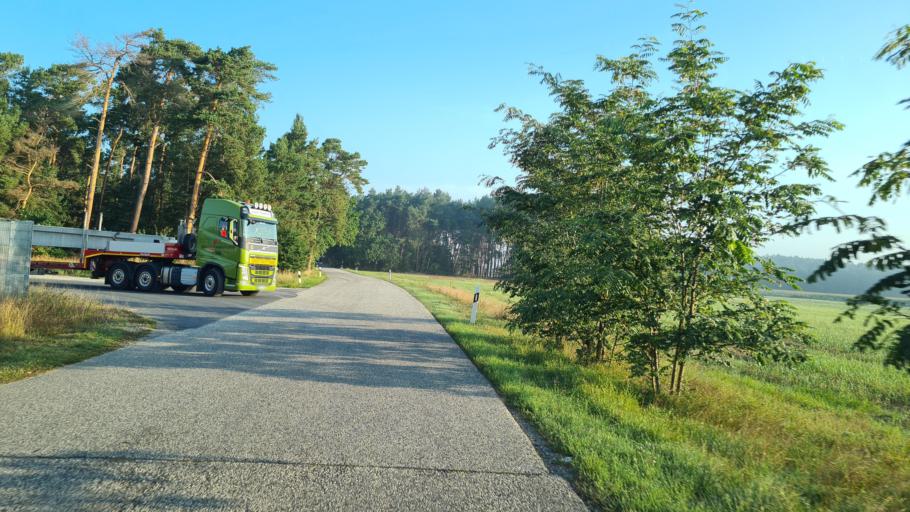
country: DE
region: Brandenburg
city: Luckenwalde
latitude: 52.1104
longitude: 13.0706
